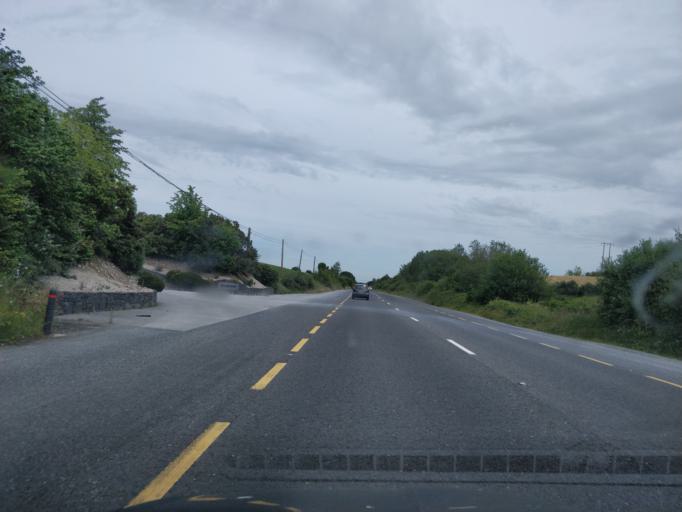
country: IE
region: Leinster
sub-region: Uibh Fhaili
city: Birr
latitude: 53.1261
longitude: -7.8714
